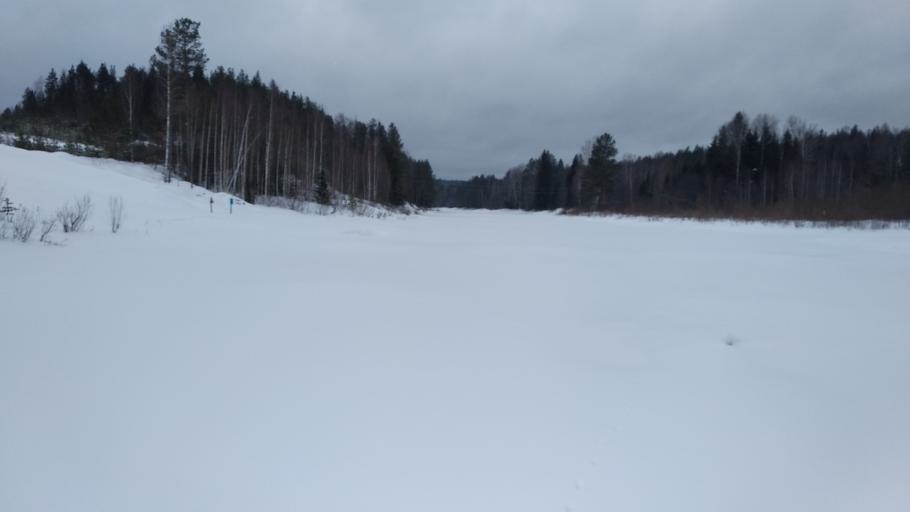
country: RU
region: Sverdlovsk
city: Rudnichnyy
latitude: 59.4413
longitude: 60.2019
